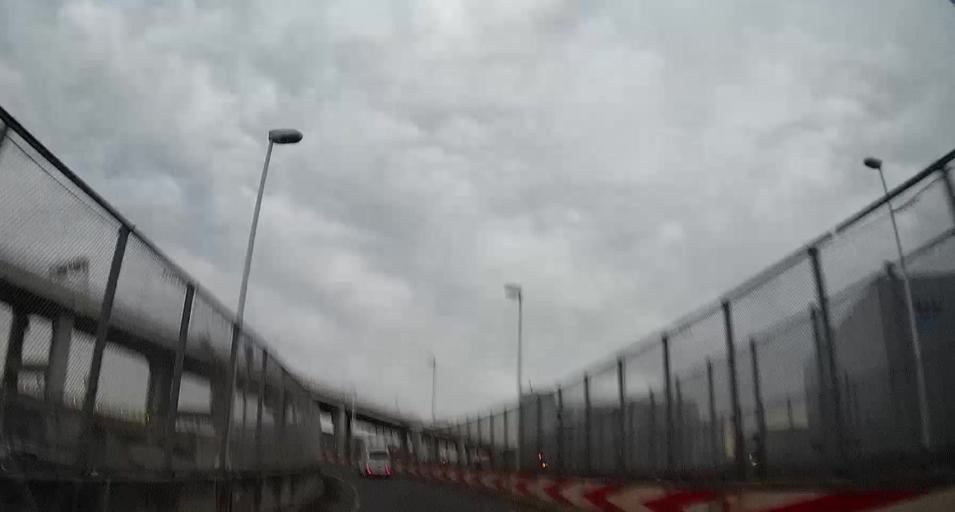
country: JP
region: Kanagawa
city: Yokohama
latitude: 35.4644
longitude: 139.6849
